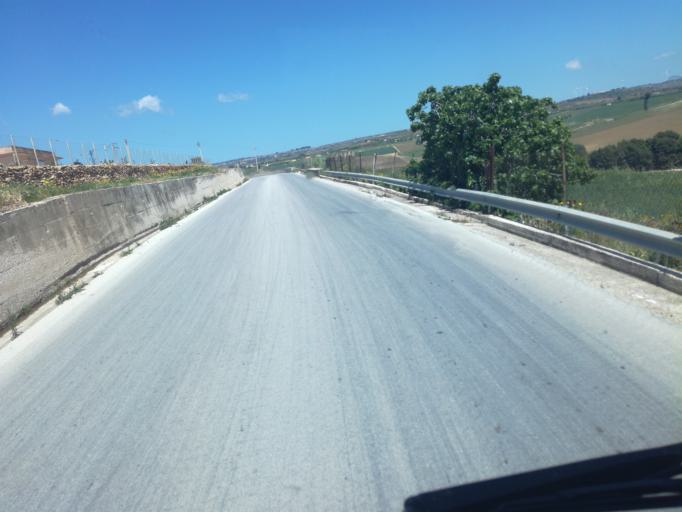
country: IT
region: Sicily
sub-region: Agrigento
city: Menfi
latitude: 37.5950
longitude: 12.9783
